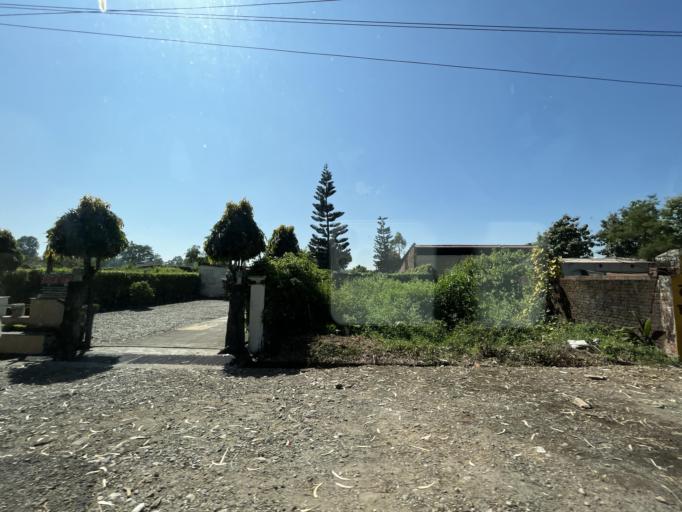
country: IN
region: Uttarakhand
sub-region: Naini Tal
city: Haldwani
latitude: 29.2108
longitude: 79.4627
